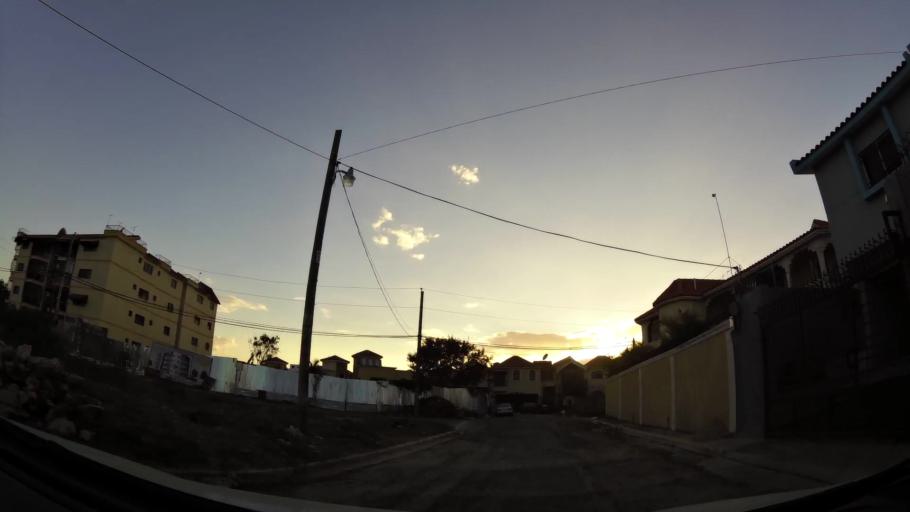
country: DO
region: Santo Domingo
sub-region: Santo Domingo
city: Santo Domingo Este
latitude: 18.4846
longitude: -69.8219
